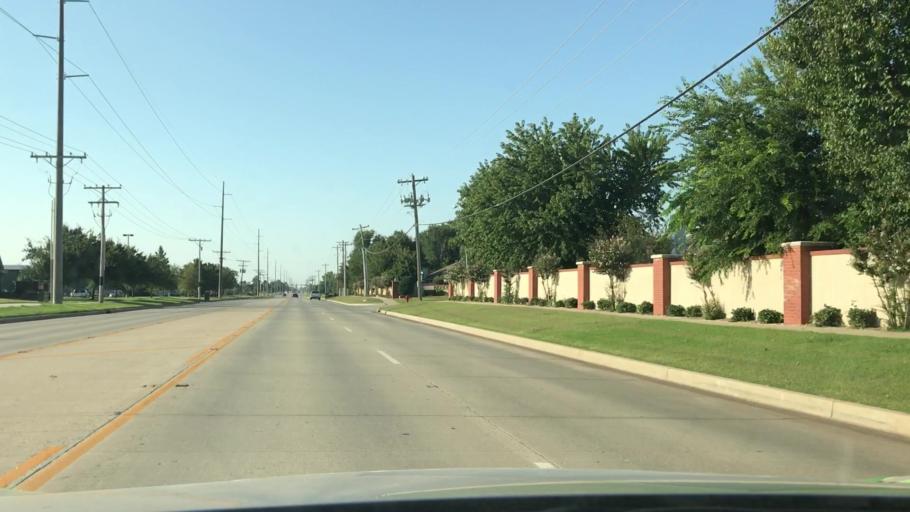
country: US
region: Oklahoma
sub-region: Cleveland County
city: Norman
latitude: 35.2529
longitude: -97.4943
